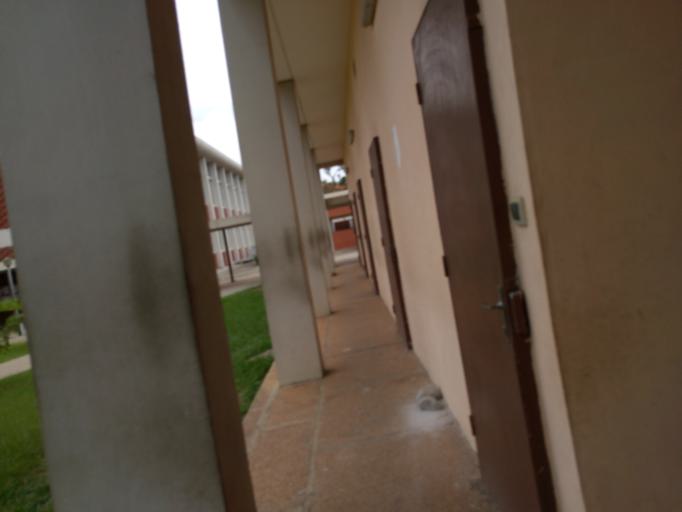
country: CI
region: Lagunes
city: Abidjan
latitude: 5.3452
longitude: -3.9876
